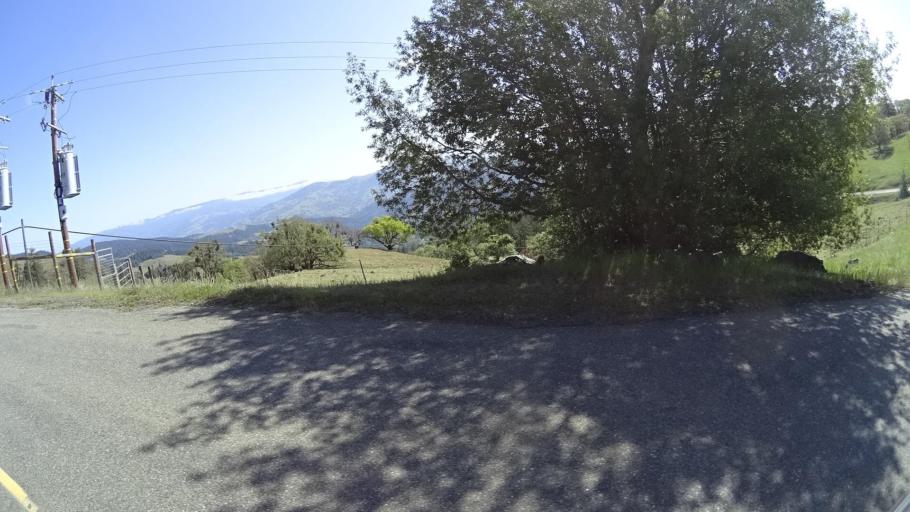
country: US
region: California
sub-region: Humboldt County
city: Redway
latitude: 40.0856
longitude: -123.6696
